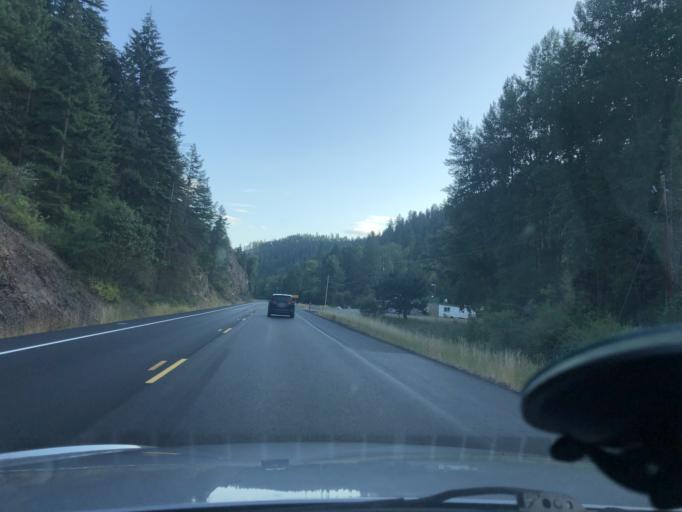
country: US
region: Washington
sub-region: Kittitas County
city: Cle Elum
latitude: 47.2237
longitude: -120.6968
